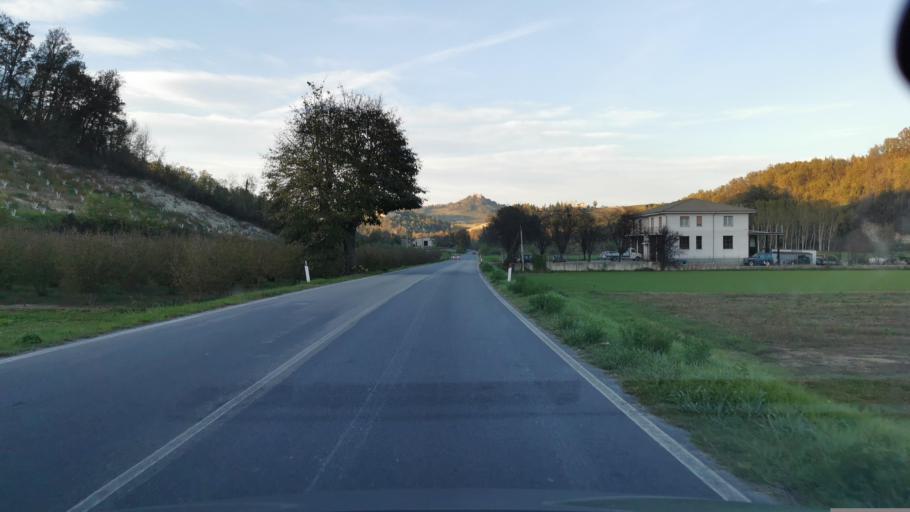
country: IT
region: Piedmont
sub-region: Provincia di Cuneo
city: Monchiero Borgonuovo
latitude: 44.5532
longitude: 7.9219
